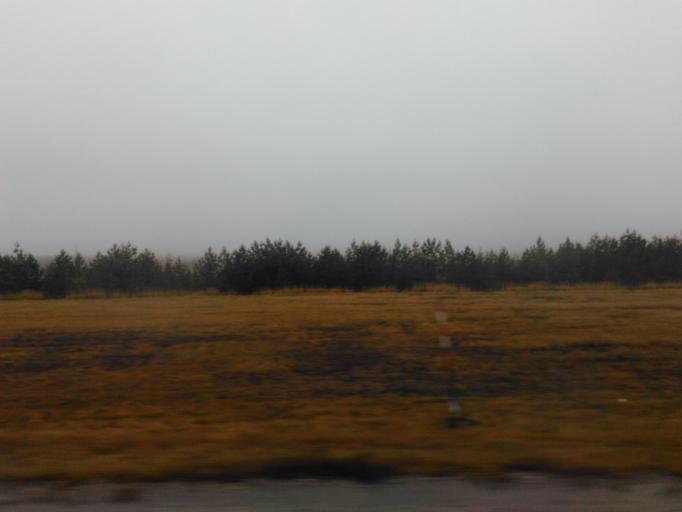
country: RU
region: Tatarstan
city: Sviyazhsk
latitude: 55.7357
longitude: 48.7807
